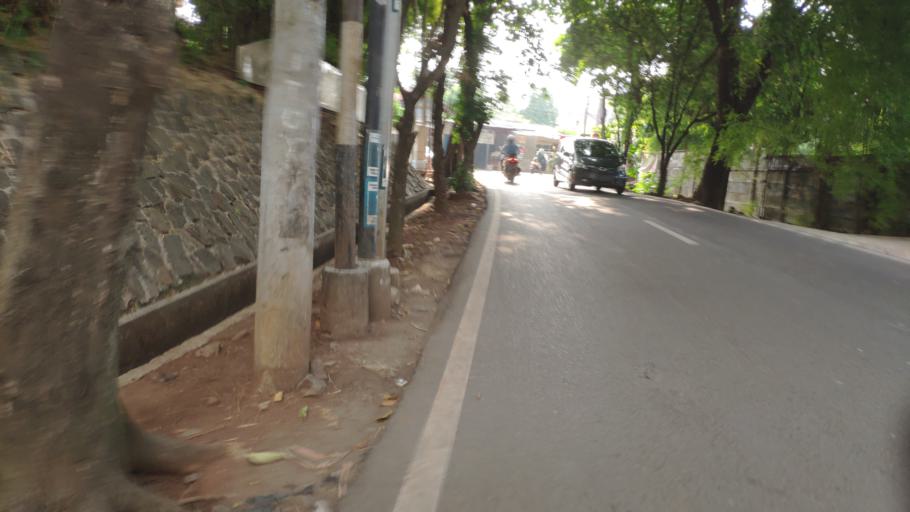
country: ID
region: West Java
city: Pamulang
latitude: -6.3044
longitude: 106.8025
